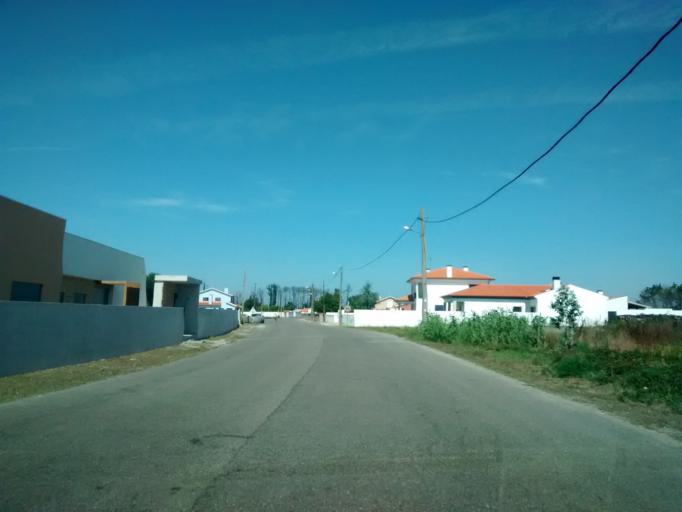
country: PT
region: Coimbra
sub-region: Mira
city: Mira
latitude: 40.4329
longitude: -8.7090
